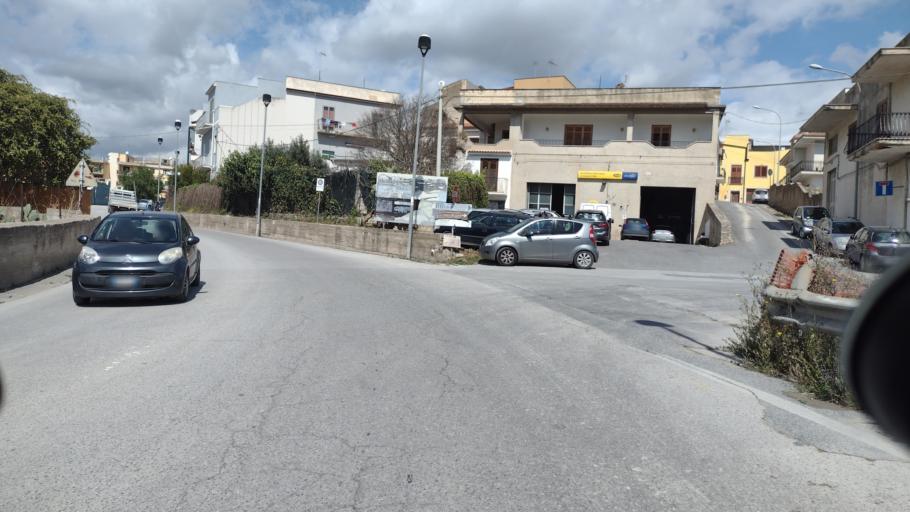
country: IT
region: Sicily
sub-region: Provincia di Siracusa
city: Noto
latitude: 36.8891
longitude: 15.0629
